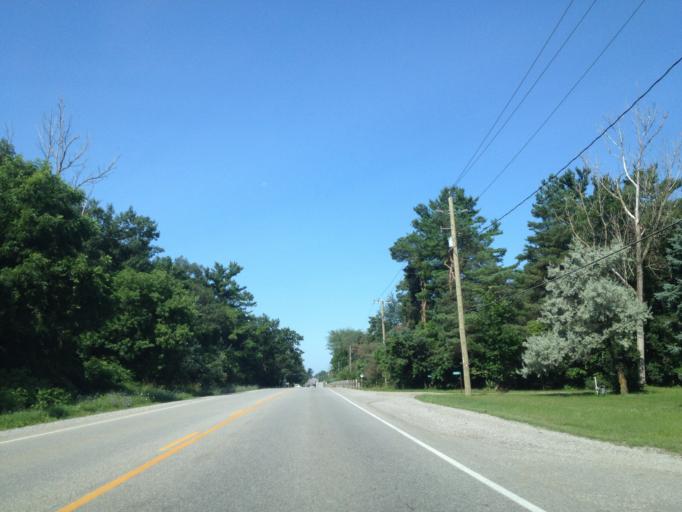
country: CA
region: Ontario
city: Norfolk County
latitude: 42.8378
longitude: -80.3510
